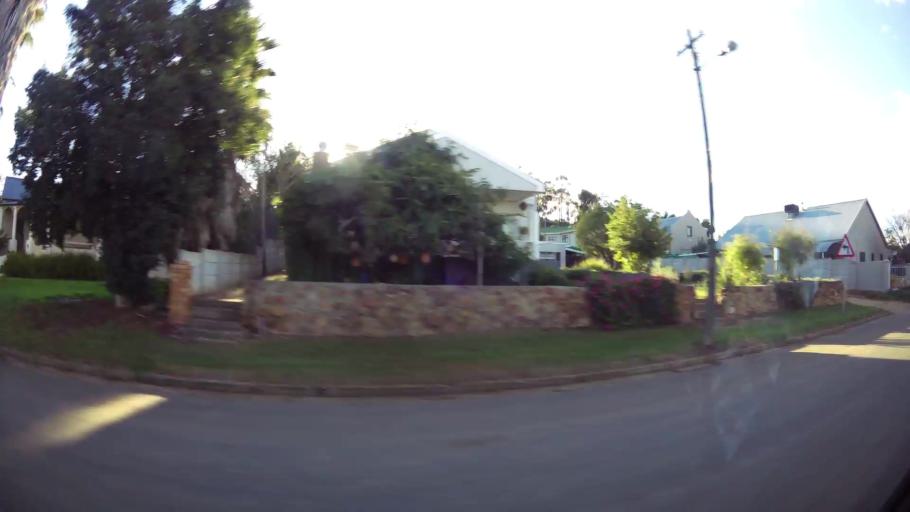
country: ZA
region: Western Cape
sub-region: Eden District Municipality
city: Riversdale
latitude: -34.0854
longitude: 20.9578
